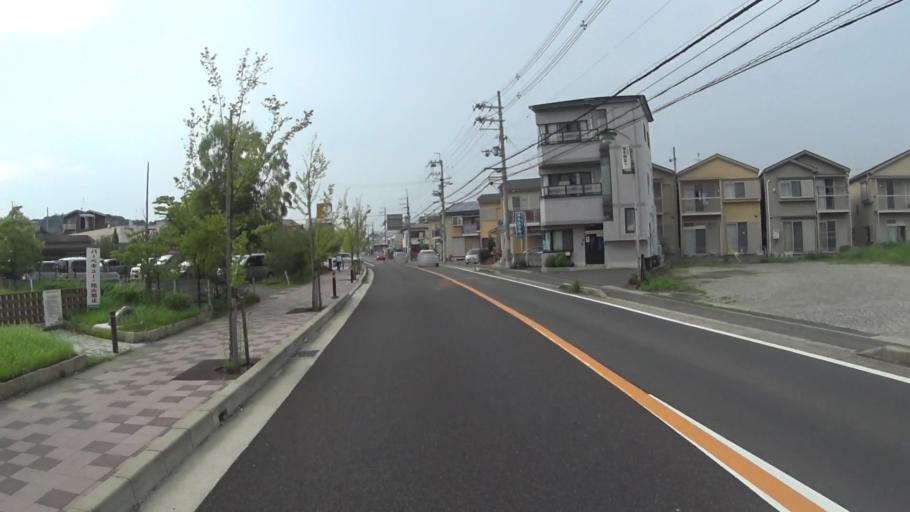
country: JP
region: Kyoto
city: Tanabe
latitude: 34.7718
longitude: 135.7905
